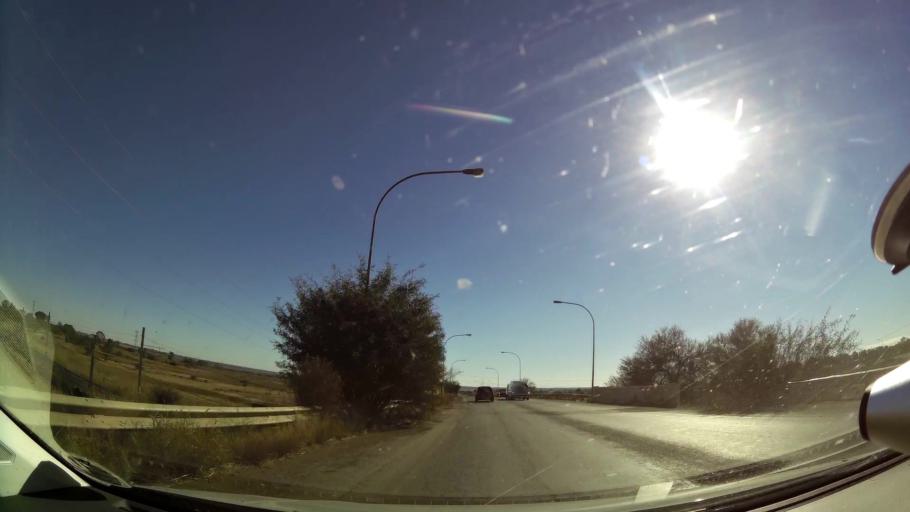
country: ZA
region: Northern Cape
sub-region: Frances Baard District Municipality
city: Kimberley
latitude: -28.7145
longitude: 24.7758
